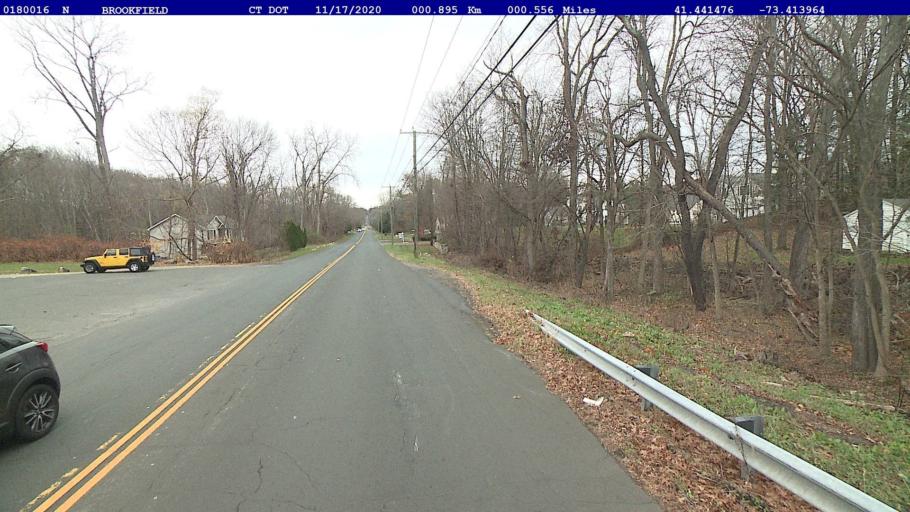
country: US
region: Connecticut
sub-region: Fairfield County
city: Danbury
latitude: 41.4415
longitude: -73.4140
